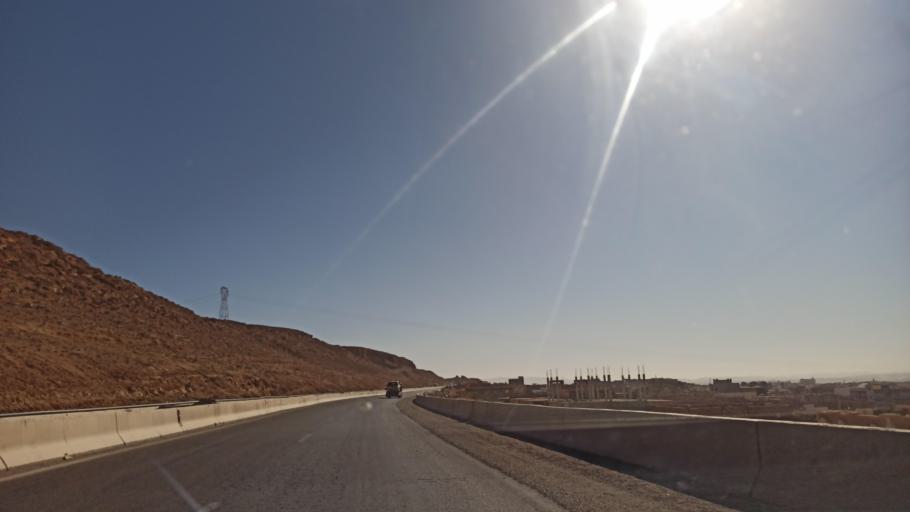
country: TN
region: Gafsa
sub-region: Gafsa Municipality
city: Gafsa
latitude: 34.4425
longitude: 8.7905
